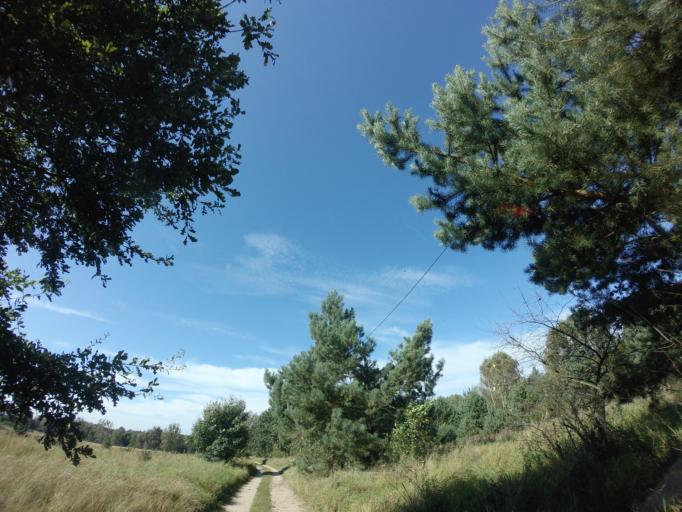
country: PL
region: West Pomeranian Voivodeship
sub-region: Powiat choszczenski
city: Recz
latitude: 53.1900
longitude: 15.5040
